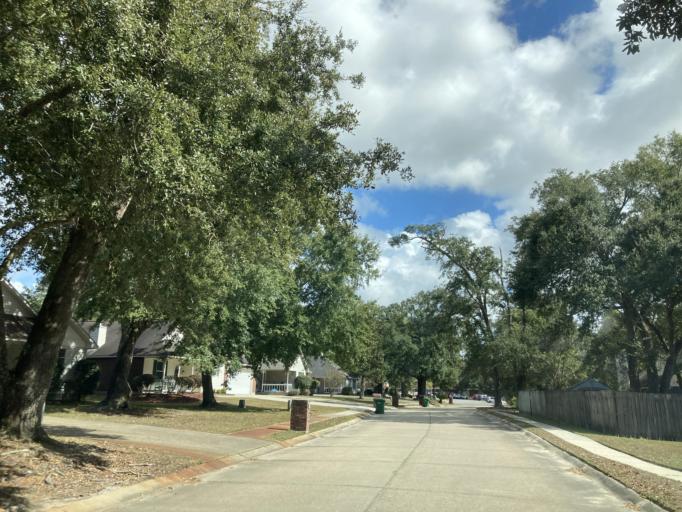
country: US
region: Mississippi
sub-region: Jackson County
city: Gulf Hills
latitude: 30.4503
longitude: -88.8318
